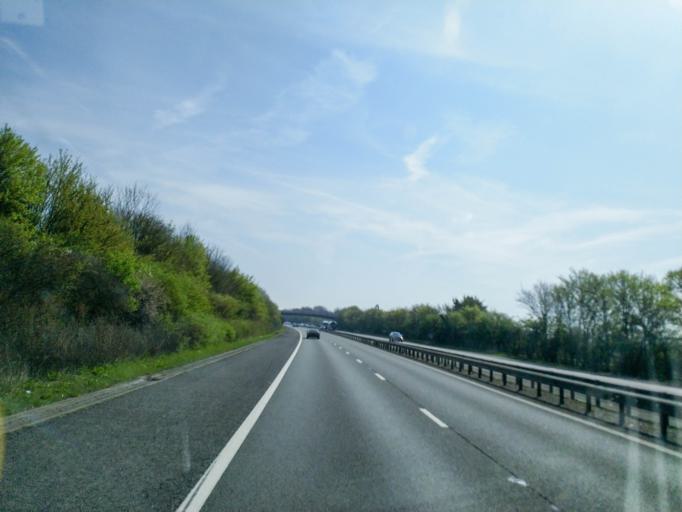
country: GB
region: England
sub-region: Kent
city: Kemsing
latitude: 51.3012
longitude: 0.2206
